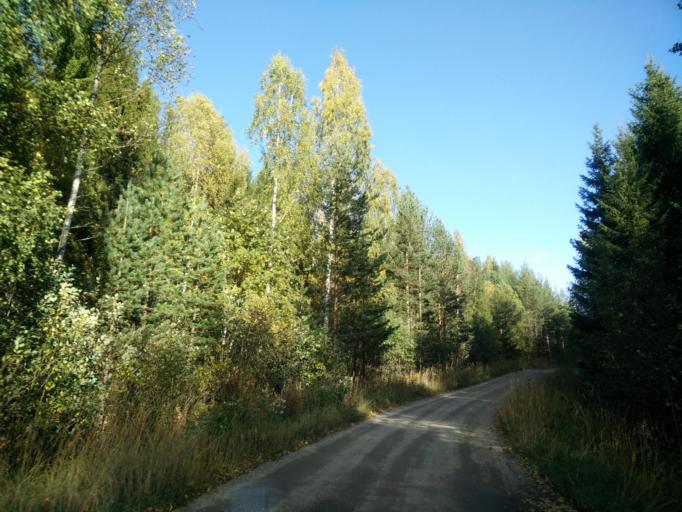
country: SE
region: Vaesternorrland
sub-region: Sundsvalls Kommun
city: Matfors
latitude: 62.3321
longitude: 16.9229
